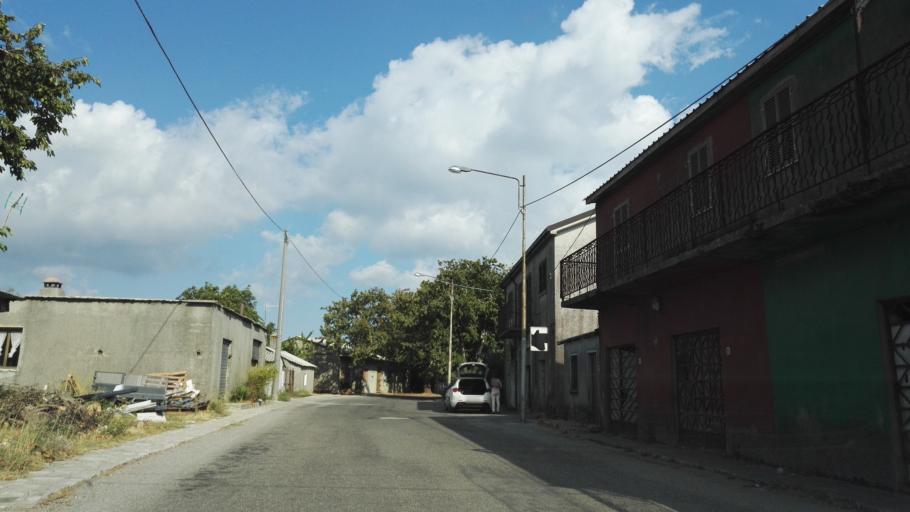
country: IT
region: Calabria
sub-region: Provincia di Vibo-Valentia
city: Nardodipace
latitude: 38.4718
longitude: 16.3446
